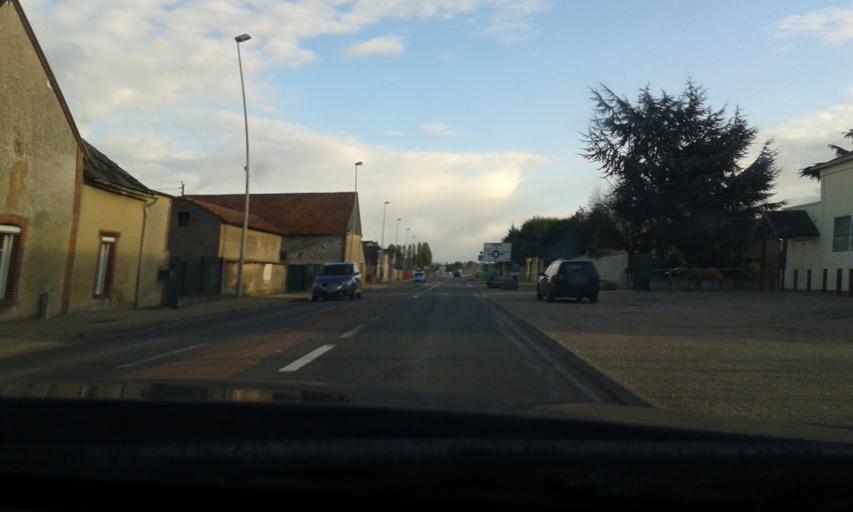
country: FR
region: Centre
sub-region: Departement d'Eure-et-Loir
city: Le Coudray
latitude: 48.4166
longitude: 1.5323
